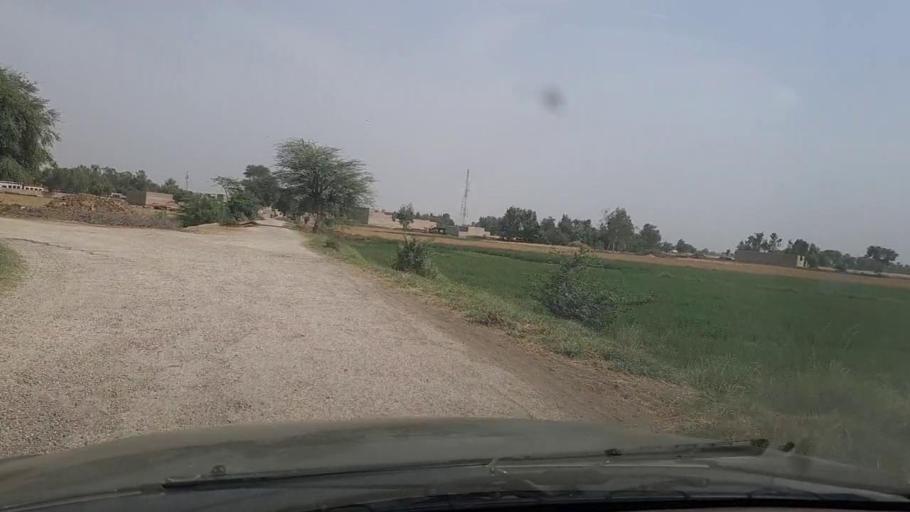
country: PK
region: Sindh
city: Chak
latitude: 27.8327
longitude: 68.7726
